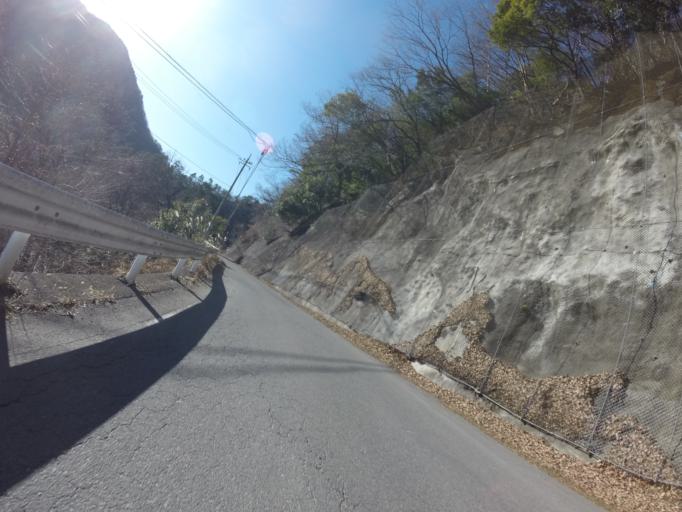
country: JP
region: Yamanashi
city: Ryuo
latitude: 35.4136
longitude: 138.3413
